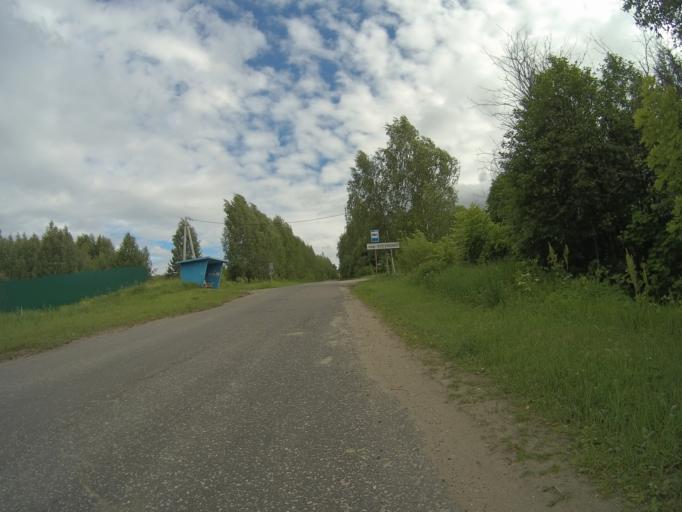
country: RU
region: Vladimir
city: Kommunar
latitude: 56.1216
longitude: 40.5042
